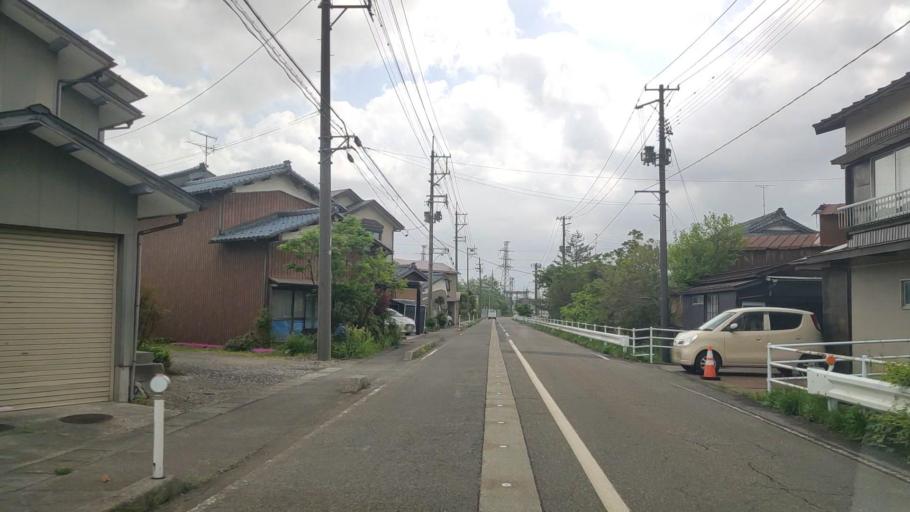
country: JP
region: Niigata
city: Gosen
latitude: 37.7361
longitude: 139.1692
